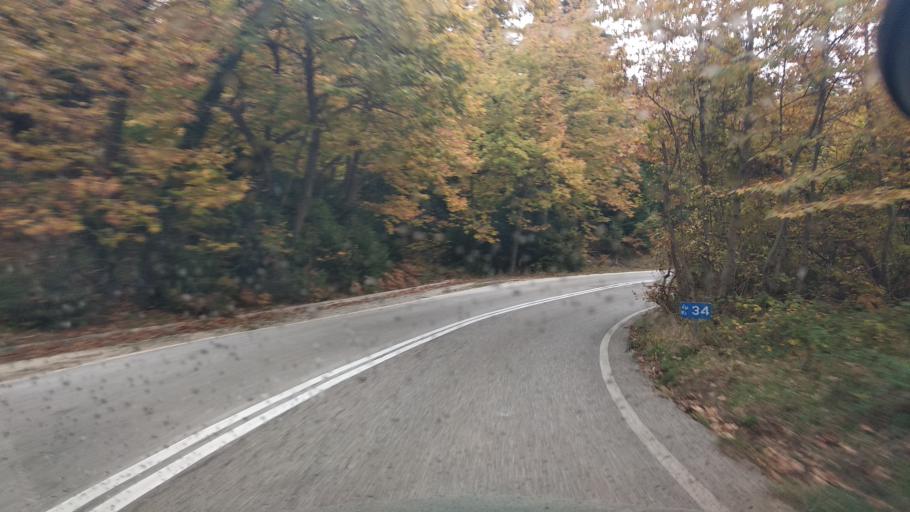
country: GR
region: Thessaly
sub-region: Trikala
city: Pyli
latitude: 39.5165
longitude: 21.5263
